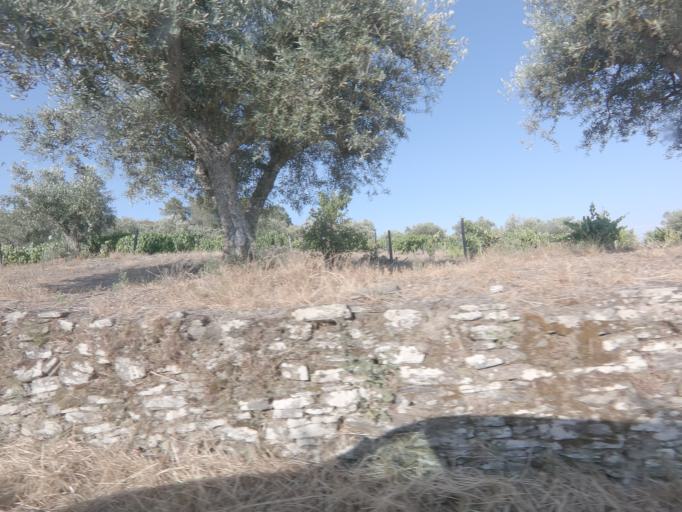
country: PT
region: Vila Real
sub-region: Sabrosa
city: Vilela
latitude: 41.1773
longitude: -7.6066
